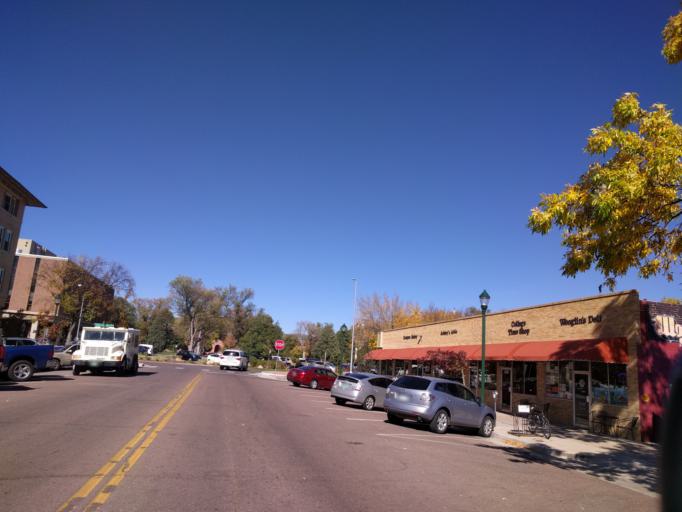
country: US
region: Colorado
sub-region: El Paso County
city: Colorado Springs
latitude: 38.8460
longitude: -104.8229
